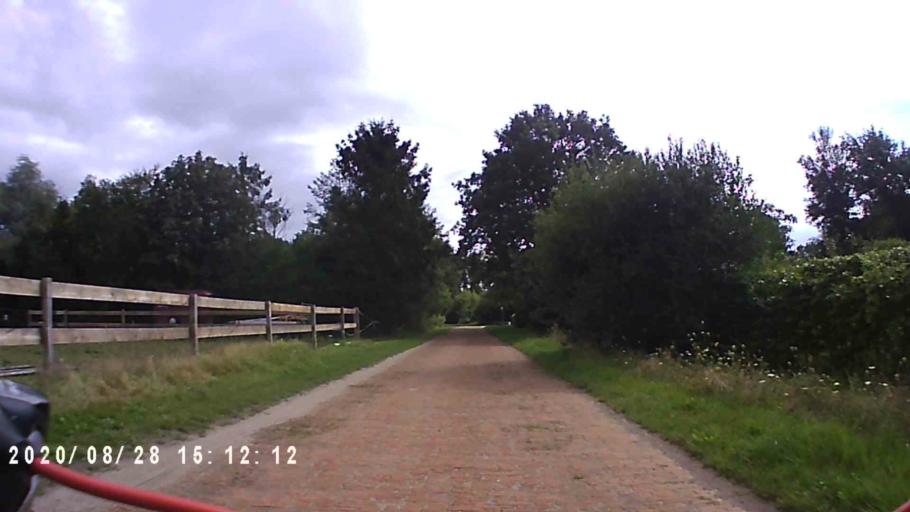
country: NL
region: Drenthe
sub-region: Gemeente Tynaarlo
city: Vries
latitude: 53.1267
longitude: 6.5750
